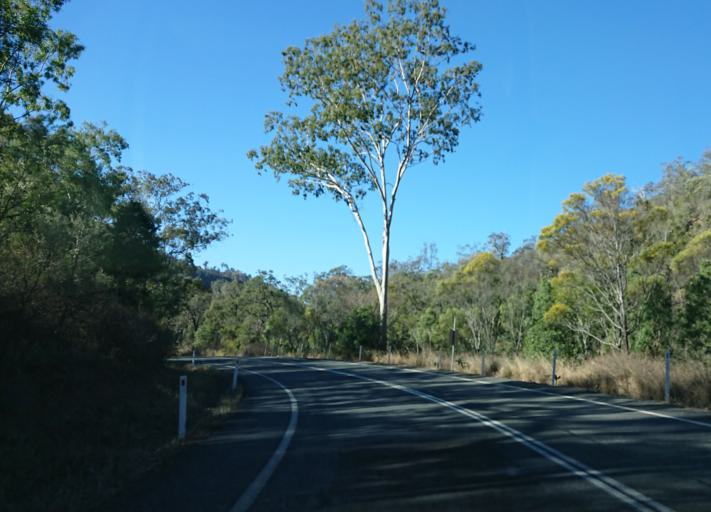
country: AU
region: Queensland
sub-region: Toowoomba
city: Top Camp
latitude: -27.7459
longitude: 152.0924
